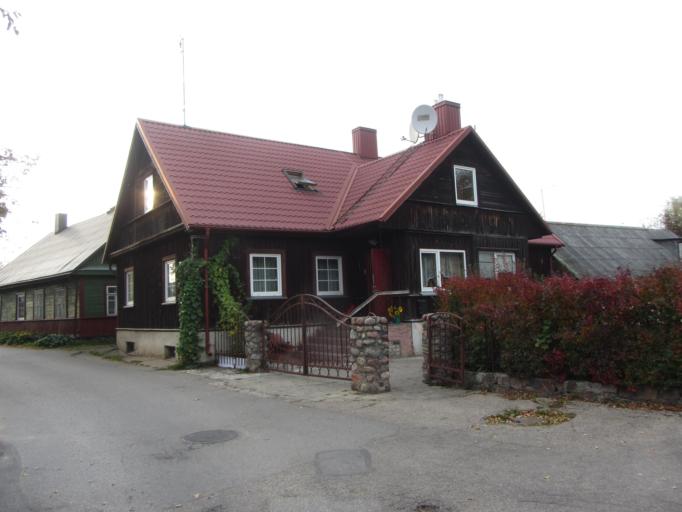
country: LT
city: Trakai
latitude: 54.6417
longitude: 24.9341
